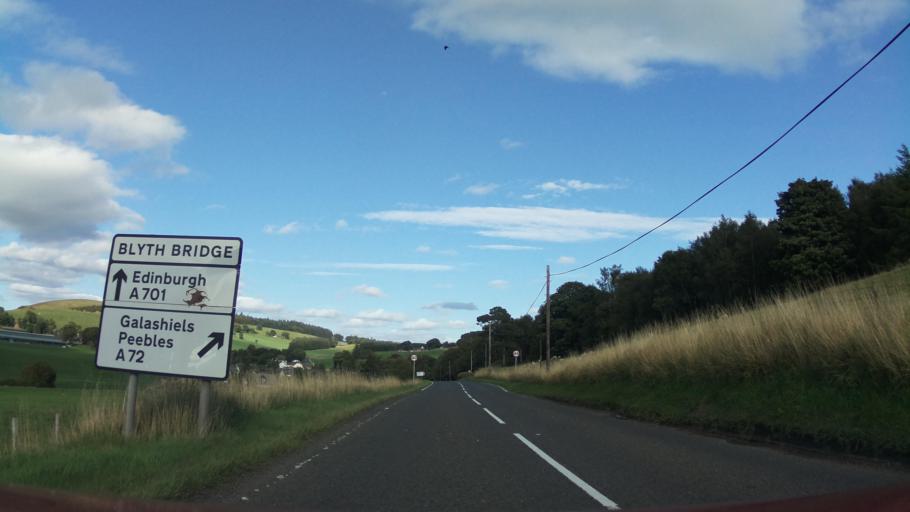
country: GB
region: Scotland
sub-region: The Scottish Borders
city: West Linton
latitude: 55.6900
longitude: -3.3882
